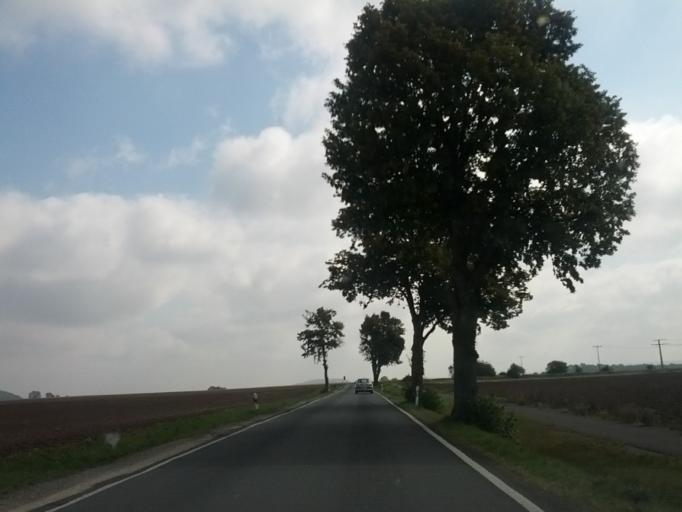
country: DE
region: Thuringia
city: Schwabhausen
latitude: 50.9163
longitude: 10.7420
